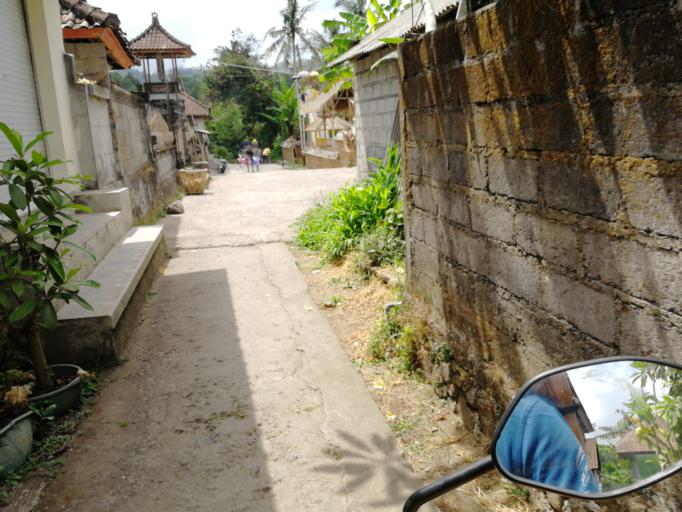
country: ID
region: Bali
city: Banjar Wangsian
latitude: -8.4695
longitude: 115.4432
